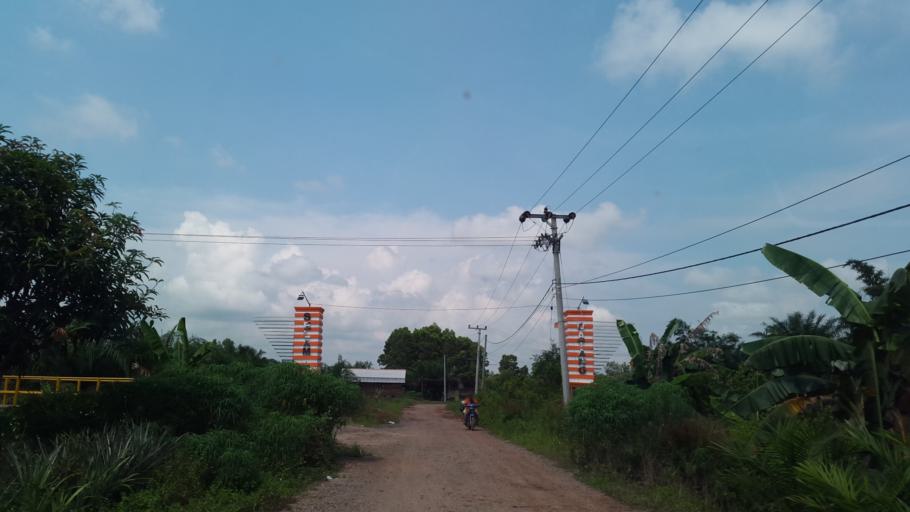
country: ID
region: South Sumatra
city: Glumbang
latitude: -3.1019
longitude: 104.5957
